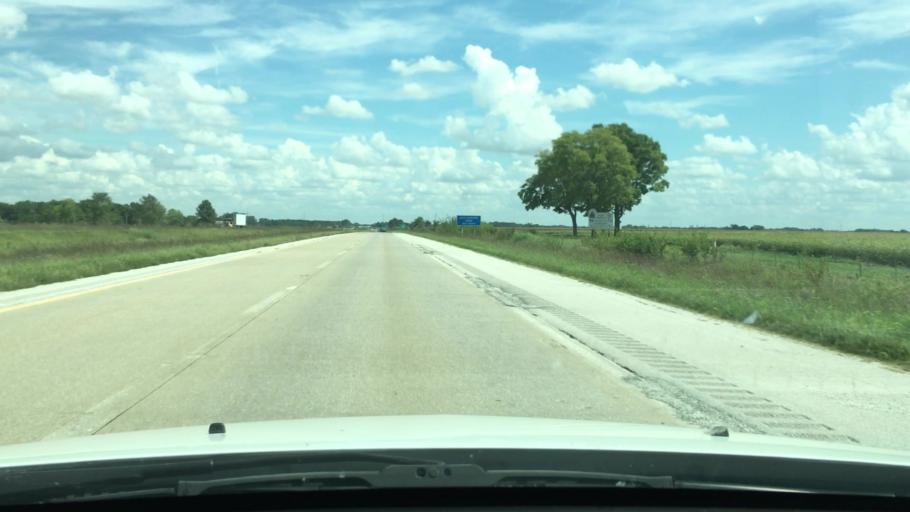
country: US
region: Illinois
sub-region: Scott County
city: Winchester
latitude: 39.6809
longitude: -90.4791
